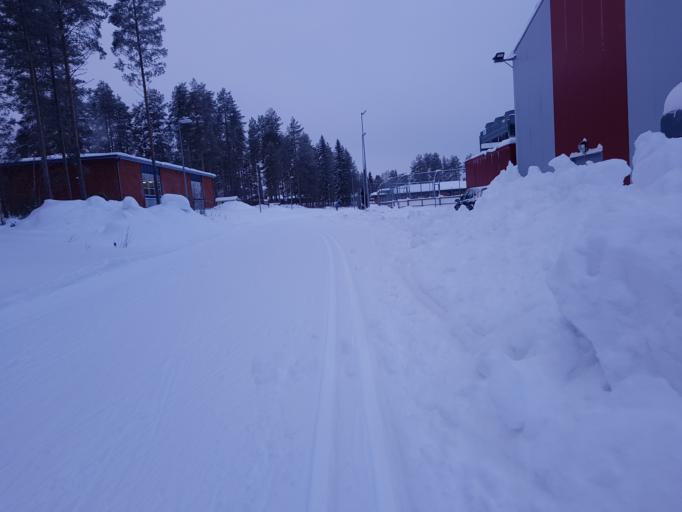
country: FI
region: Kainuu
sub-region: Kehys-Kainuu
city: Kuhmo
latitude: 64.1175
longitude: 29.5197
